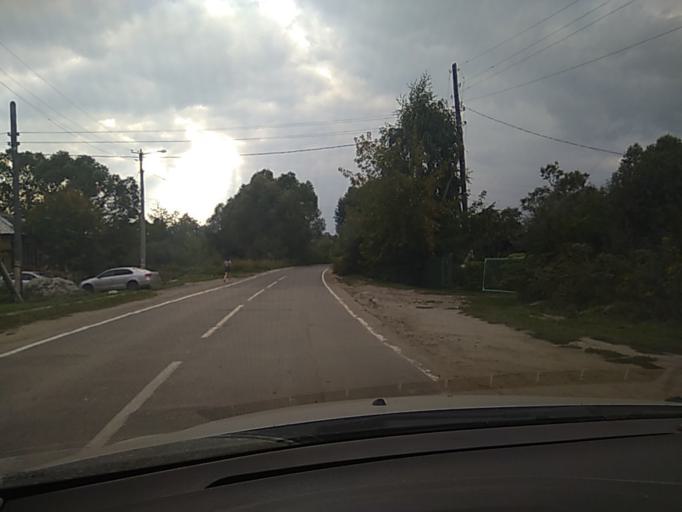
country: RU
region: Chelyabinsk
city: Kyshtym
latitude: 55.6969
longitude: 60.5451
